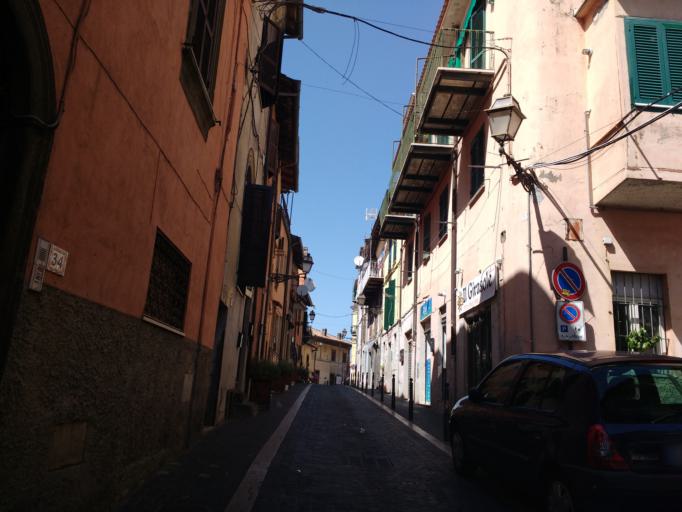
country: IT
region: Latium
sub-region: Citta metropolitana di Roma Capitale
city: Rocca di Papa
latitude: 41.7601
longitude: 12.7088
